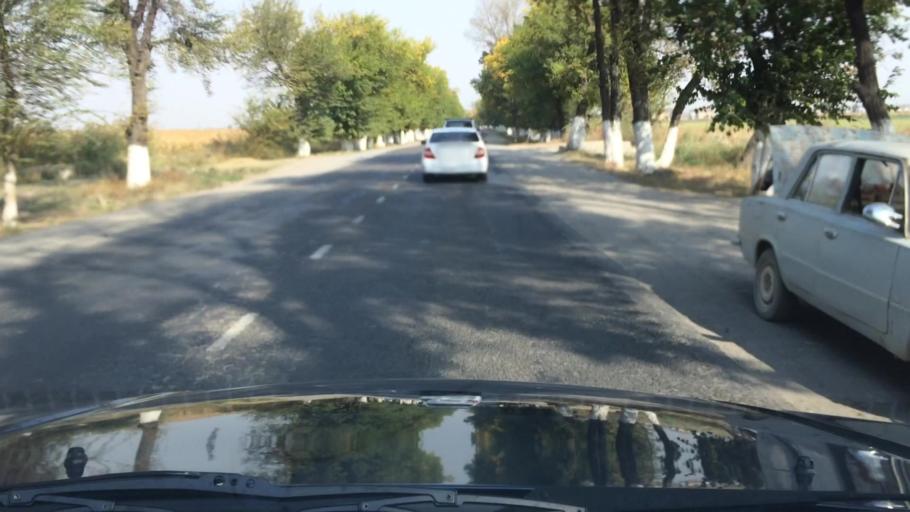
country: KG
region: Chuy
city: Lebedinovka
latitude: 42.9043
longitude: 74.6860
